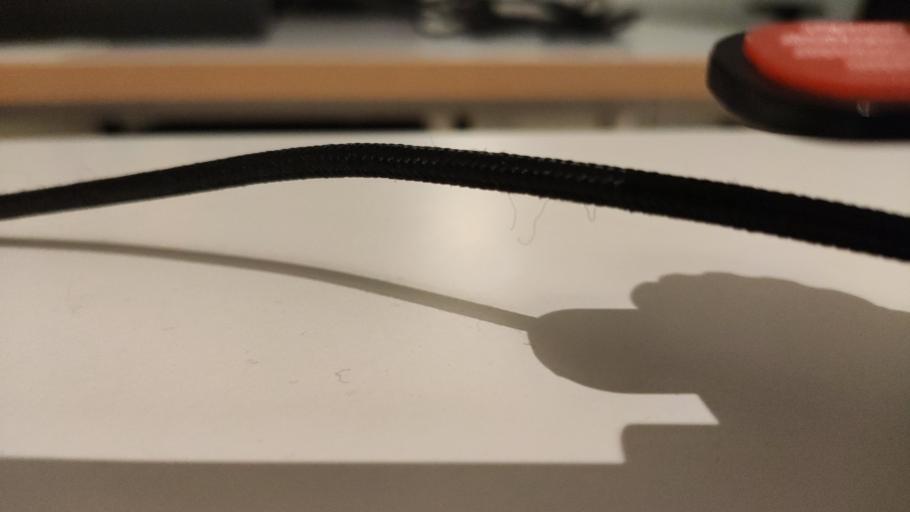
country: RU
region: Moskovskaya
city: Rogachevo
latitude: 56.4133
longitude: 37.2203
